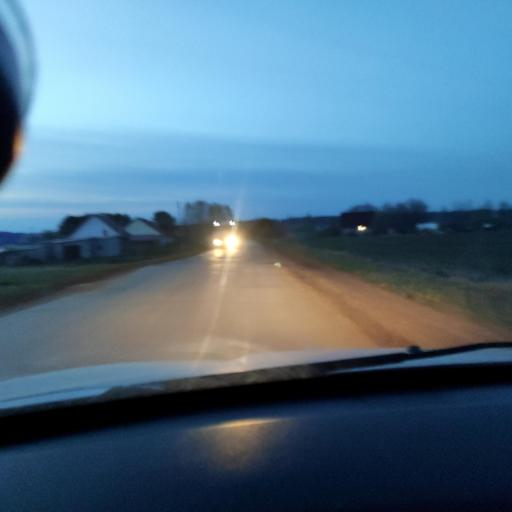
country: RU
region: Perm
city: Kukushtan
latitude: 57.4728
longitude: 56.5124
